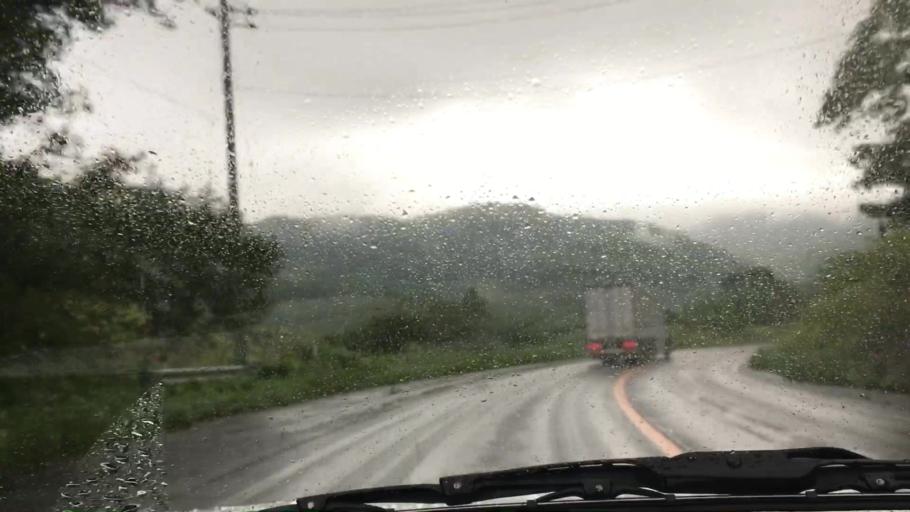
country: JP
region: Hokkaido
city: Niseko Town
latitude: 42.5952
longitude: 140.5893
